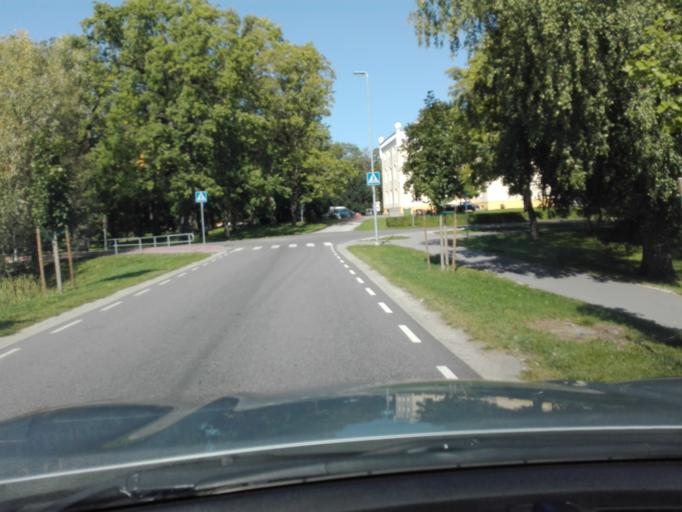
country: EE
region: Raplamaa
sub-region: Rapla vald
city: Rapla
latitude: 59.0223
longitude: 24.7643
